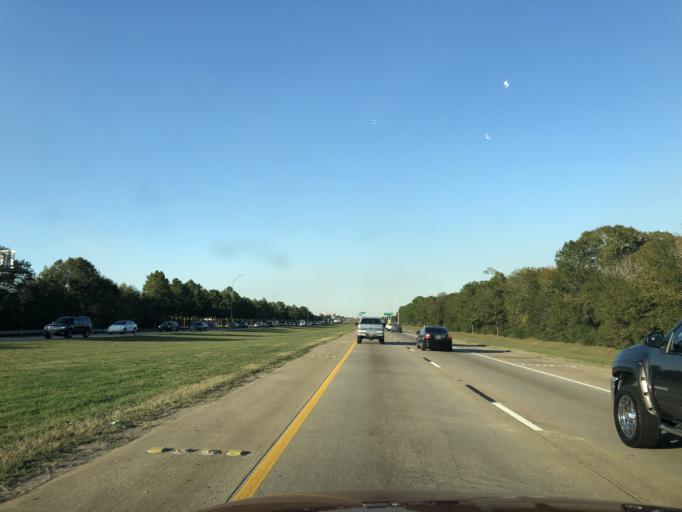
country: US
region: Texas
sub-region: Fort Bend County
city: Cinco Ranch
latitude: 29.7254
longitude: -95.7727
